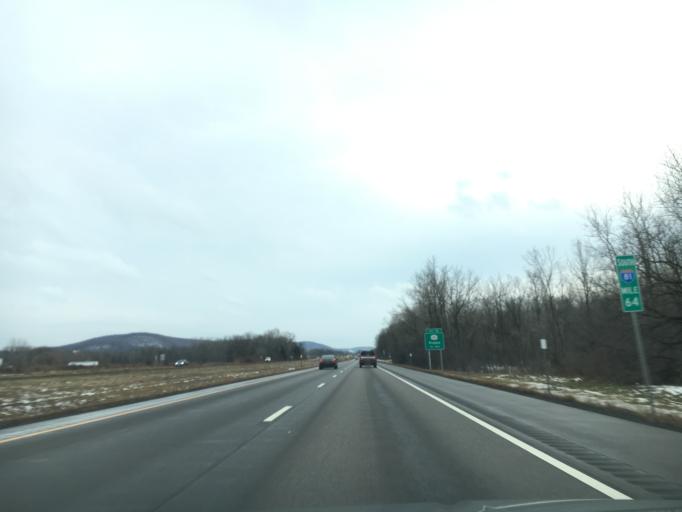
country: US
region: New York
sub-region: Cortland County
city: Homer
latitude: 42.7566
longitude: -76.1351
